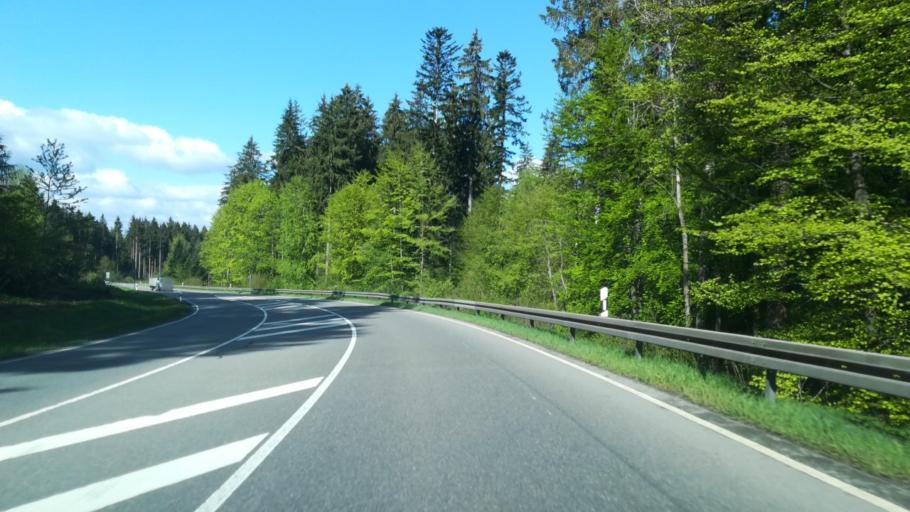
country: DE
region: Baden-Wuerttemberg
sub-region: Freiburg Region
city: Blumberg
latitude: 47.8233
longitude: 8.5695
